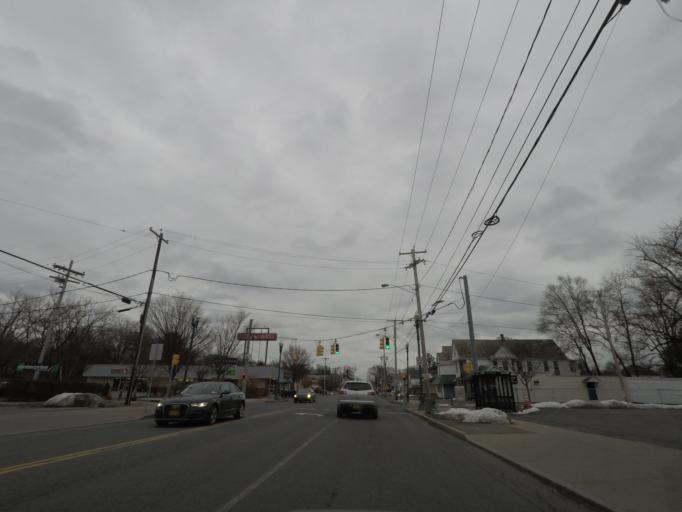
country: US
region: New York
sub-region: Schenectady County
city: Schenectady
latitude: 42.7922
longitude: -73.9174
